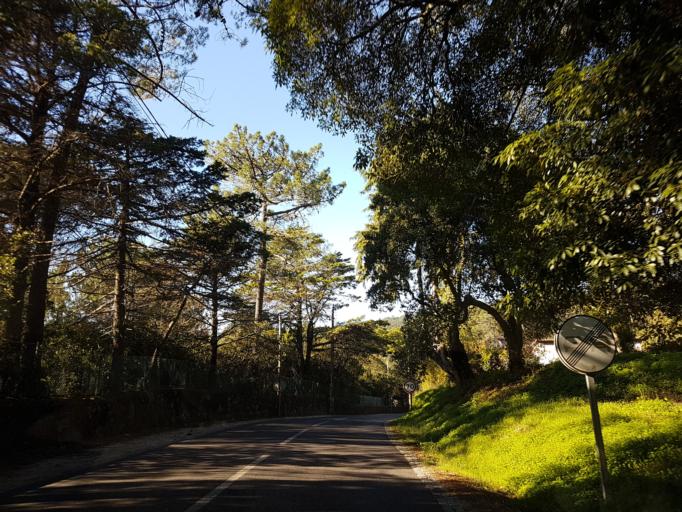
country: PT
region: Lisbon
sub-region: Sintra
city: Sintra
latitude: 38.7681
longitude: -9.3936
